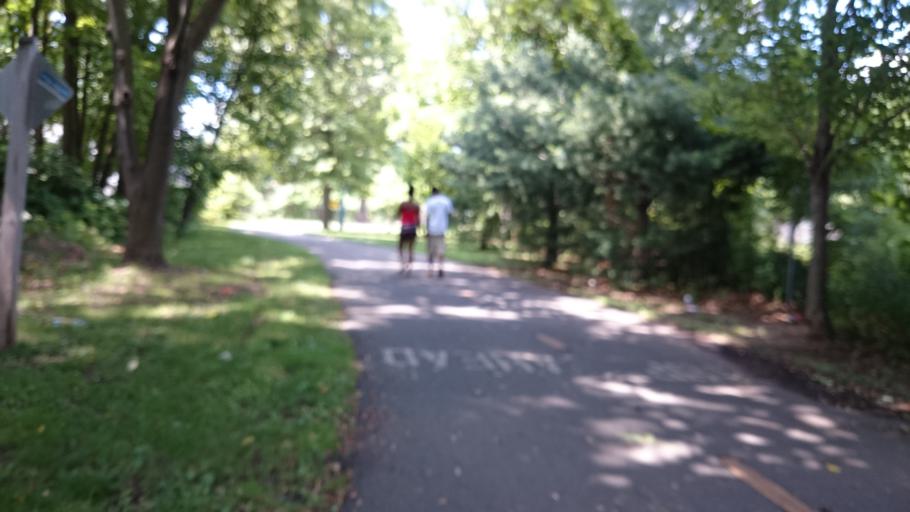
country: US
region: Connecticut
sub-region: New Haven County
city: New Haven
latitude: 41.3305
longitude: -72.9335
